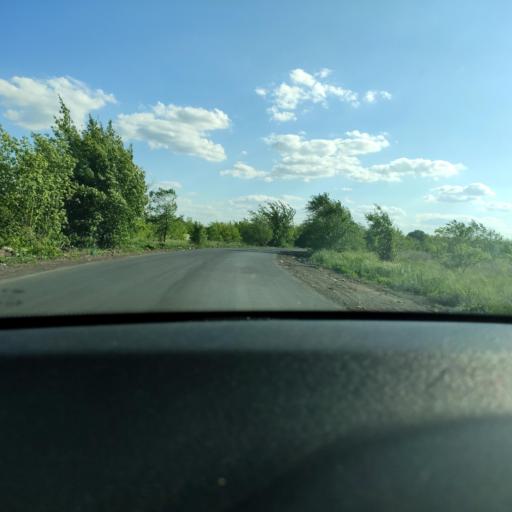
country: RU
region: Samara
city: Smyshlyayevka
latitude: 53.2467
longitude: 50.3654
